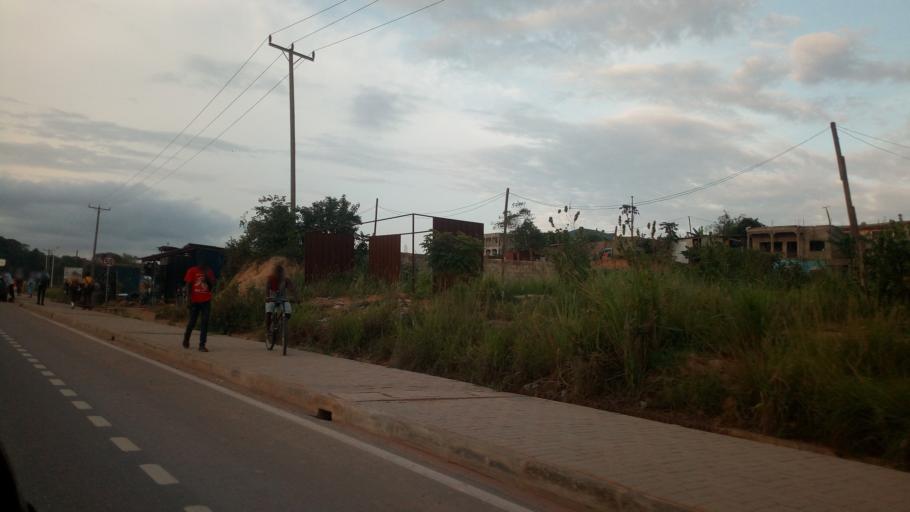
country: GH
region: Western
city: Sekondi-Takoradi
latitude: 4.9484
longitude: -1.7628
